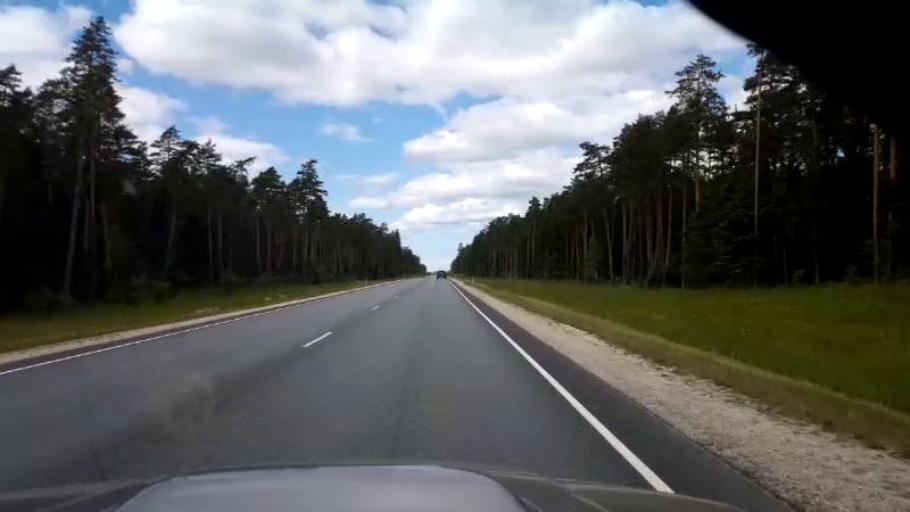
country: EE
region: Raplamaa
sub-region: Maerjamaa vald
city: Marjamaa
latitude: 59.0138
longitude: 24.4546
